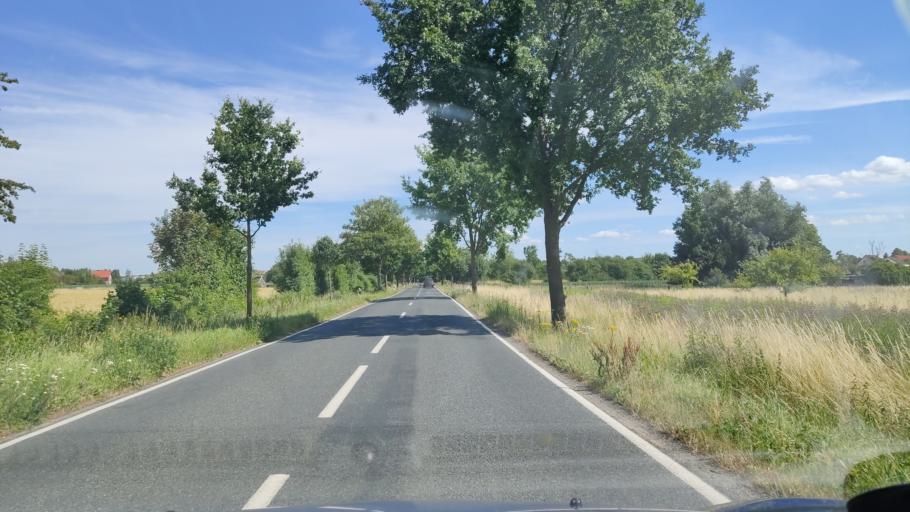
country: DE
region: Lower Saxony
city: Ronnenberg
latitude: 52.3244
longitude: 9.6437
